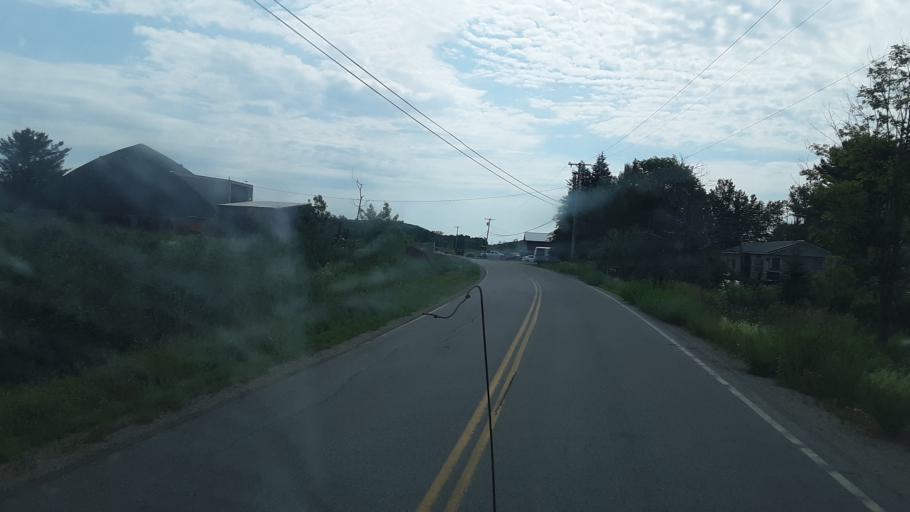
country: US
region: Maine
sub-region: Waldo County
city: Frankfort
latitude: 44.6146
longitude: -68.9384
